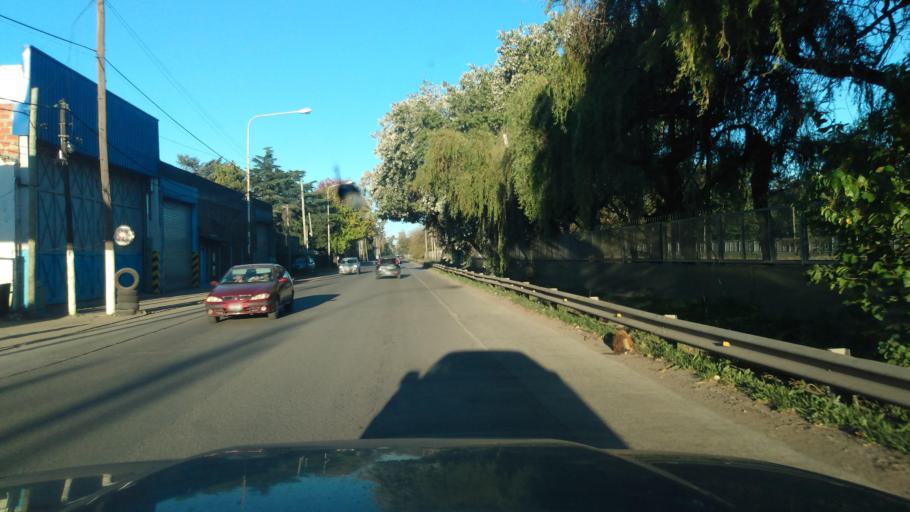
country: AR
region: Buenos Aires
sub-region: Partido de Merlo
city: Merlo
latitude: -34.6404
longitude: -58.8253
